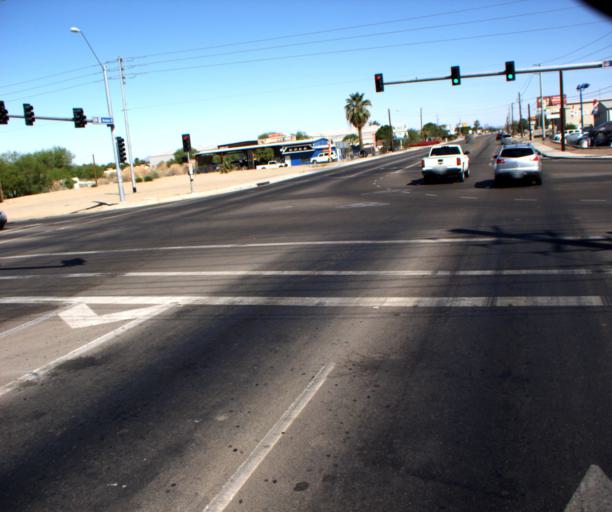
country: US
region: Arizona
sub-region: Yuma County
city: Yuma
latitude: 32.6692
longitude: -114.6500
